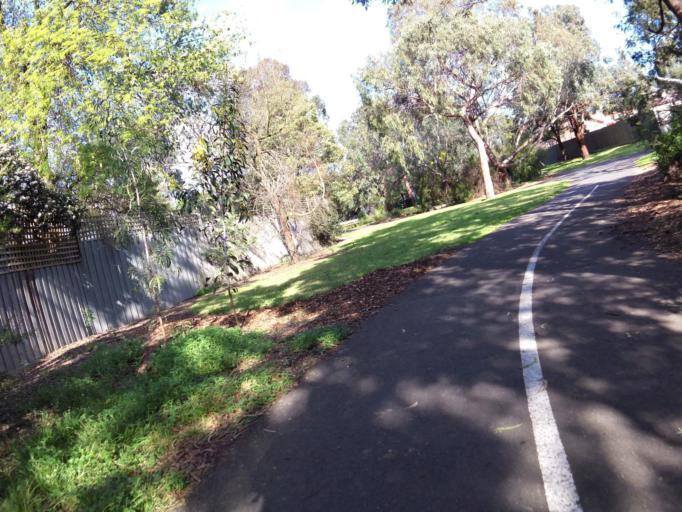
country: AU
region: Victoria
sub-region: Whitehorse
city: Box Hill North
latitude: -37.8010
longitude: 145.1203
